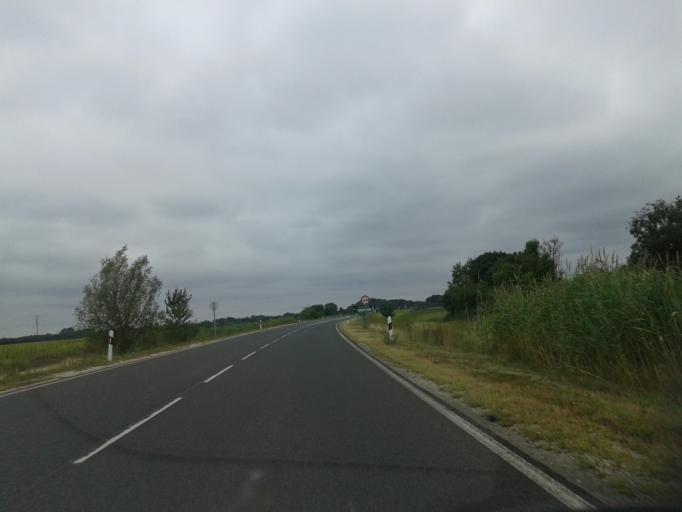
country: HU
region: Bacs-Kiskun
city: Harta
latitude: 46.7158
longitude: 19.0224
